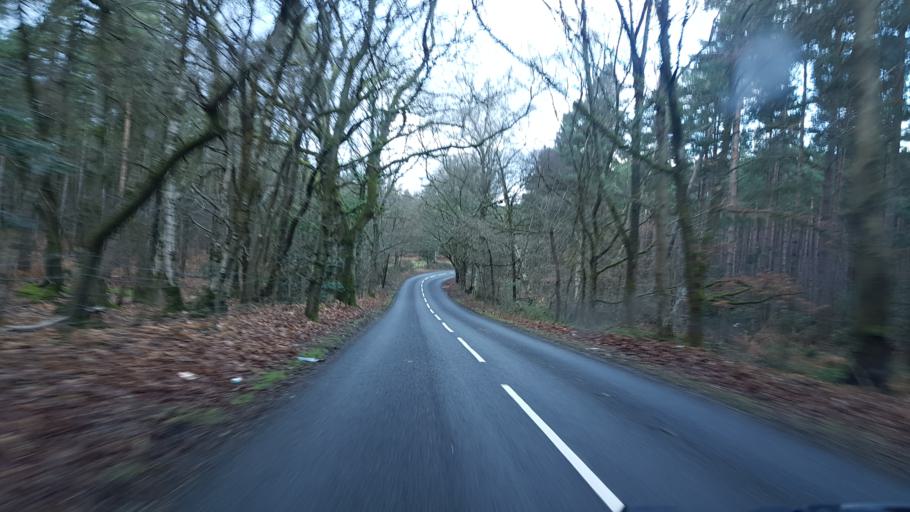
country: GB
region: England
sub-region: Surrey
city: Elstead
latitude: 51.1979
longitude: -0.7173
